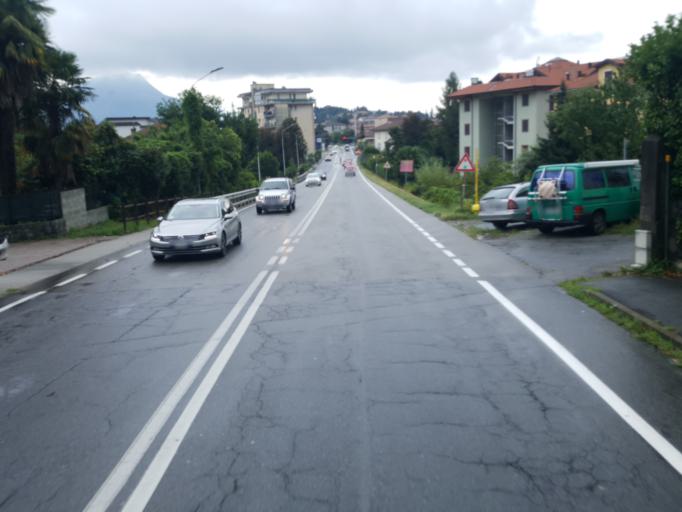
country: IT
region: Piedmont
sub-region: Provincia Verbano-Cusio-Ossola
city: Verbania
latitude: 45.9318
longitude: 8.5429
